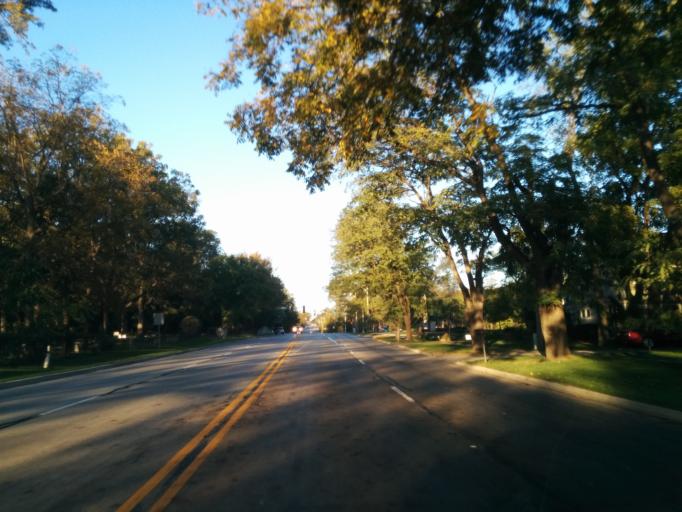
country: US
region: Illinois
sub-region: DuPage County
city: Glen Ellyn
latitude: 41.8903
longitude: -88.0542
